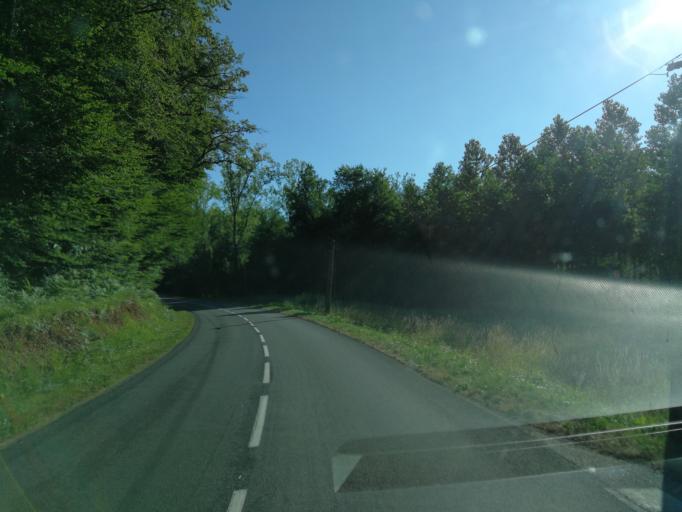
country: FR
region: Midi-Pyrenees
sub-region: Departement du Lot
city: Prayssac
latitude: 44.5935
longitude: 1.1738
